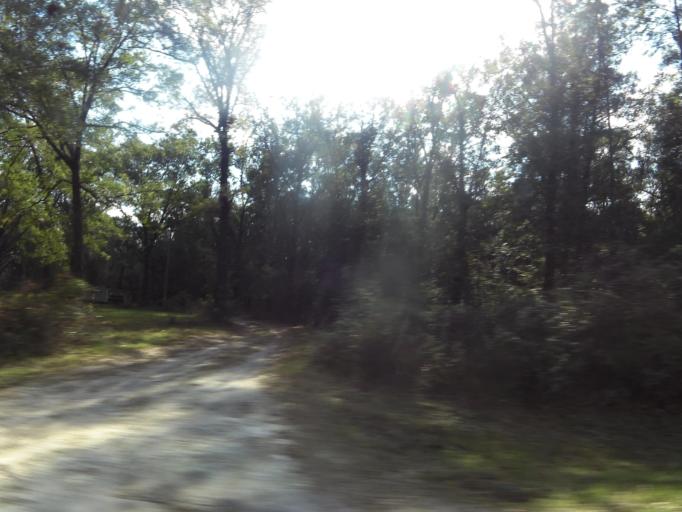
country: US
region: Florida
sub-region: Duval County
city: Baldwin
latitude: 30.1578
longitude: -81.9817
